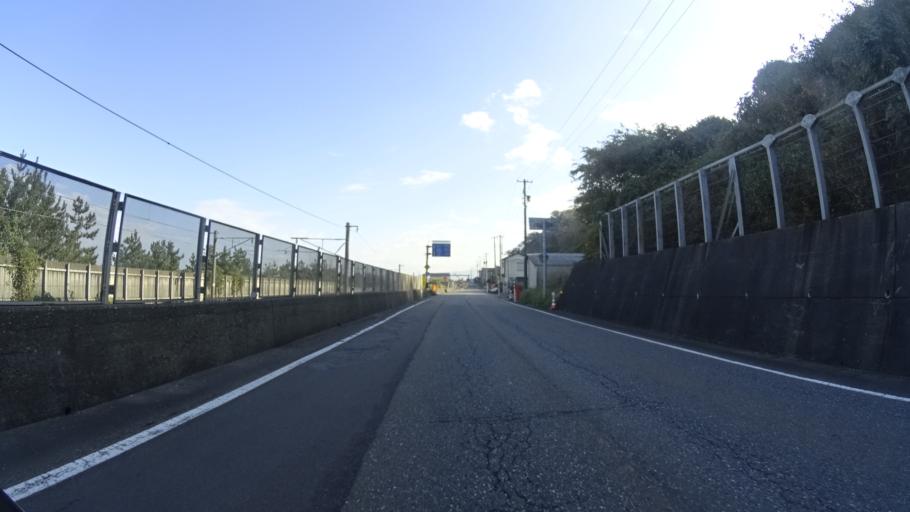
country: JP
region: Niigata
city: Itoigawa
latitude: 37.0215
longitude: 137.7839
